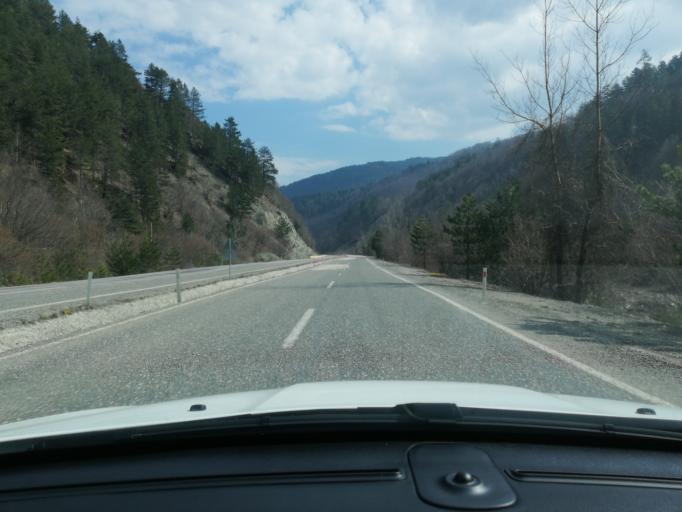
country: TR
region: Kastamonu
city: Kuzyaka
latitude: 41.1303
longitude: 33.7703
